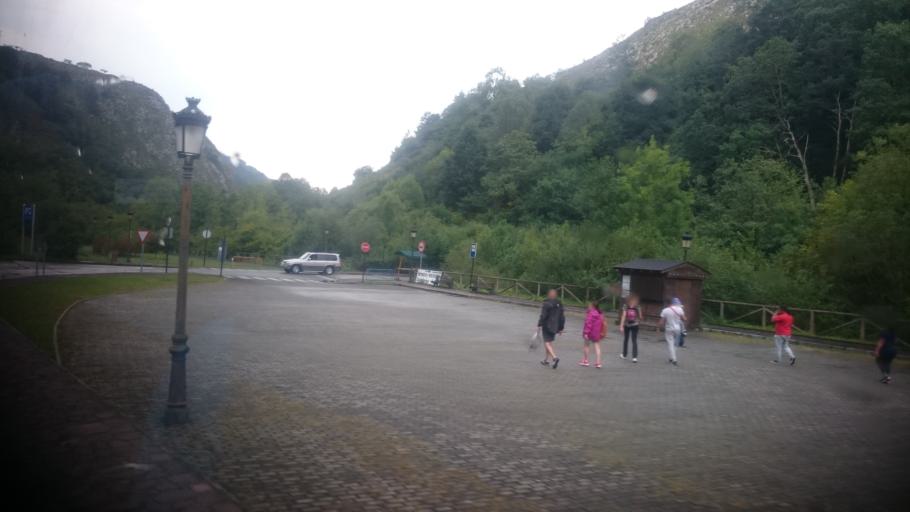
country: ES
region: Asturias
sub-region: Province of Asturias
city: Cangas de Onis
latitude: 43.3150
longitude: -5.0685
